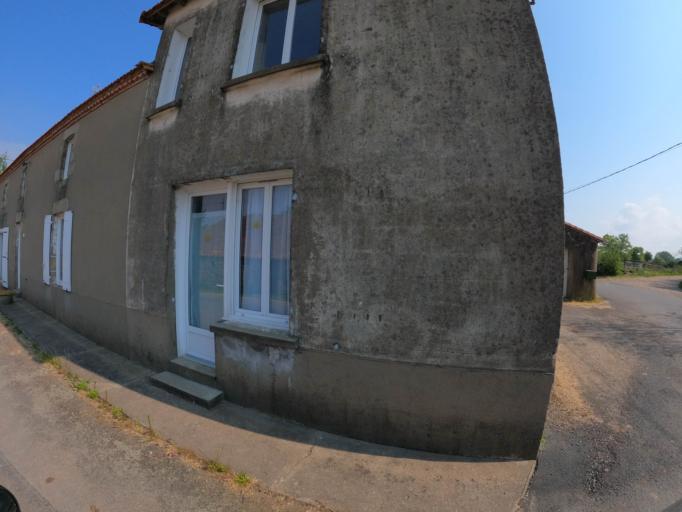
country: FR
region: Pays de la Loire
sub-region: Departement de la Vendee
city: Treize-Septiers
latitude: 47.0010
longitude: -1.2281
